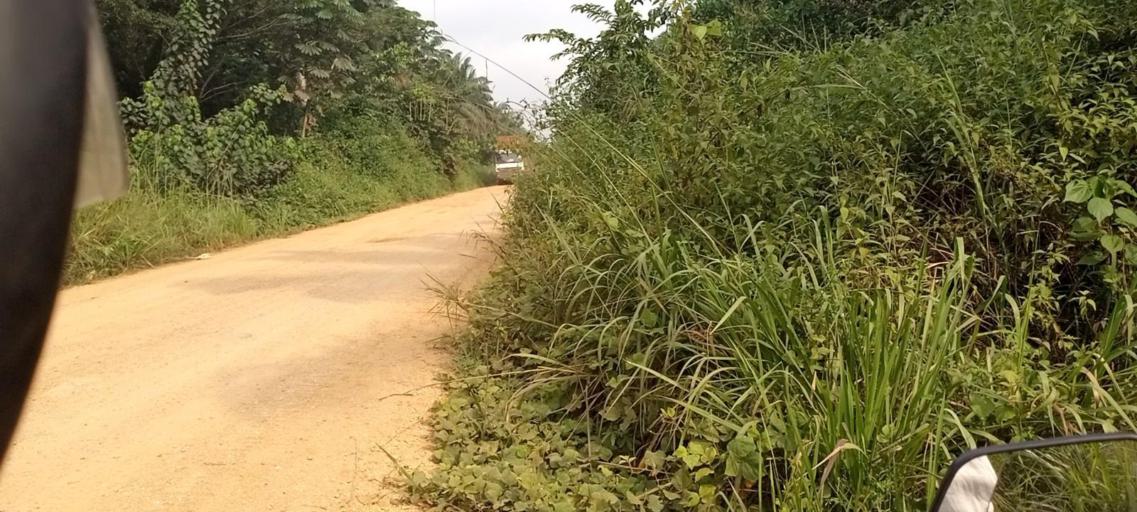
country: CD
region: Eastern Province
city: Kisangani
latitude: 0.2271
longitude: 25.5068
